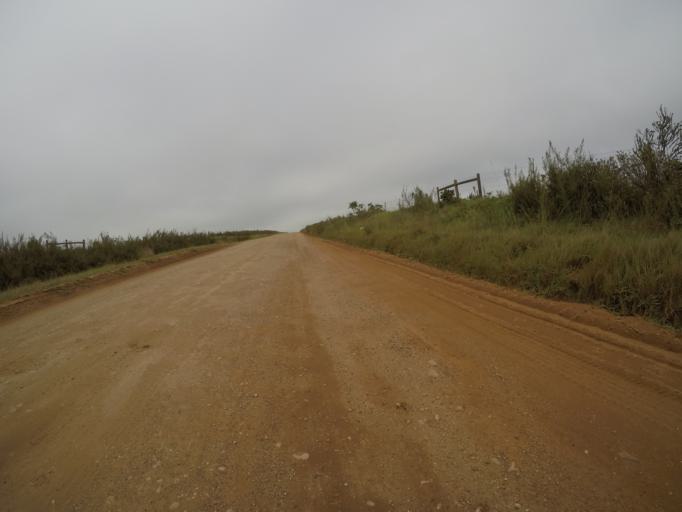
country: ZA
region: Eastern Cape
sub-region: Cacadu District Municipality
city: Kareedouw
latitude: -34.0292
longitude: 24.2433
